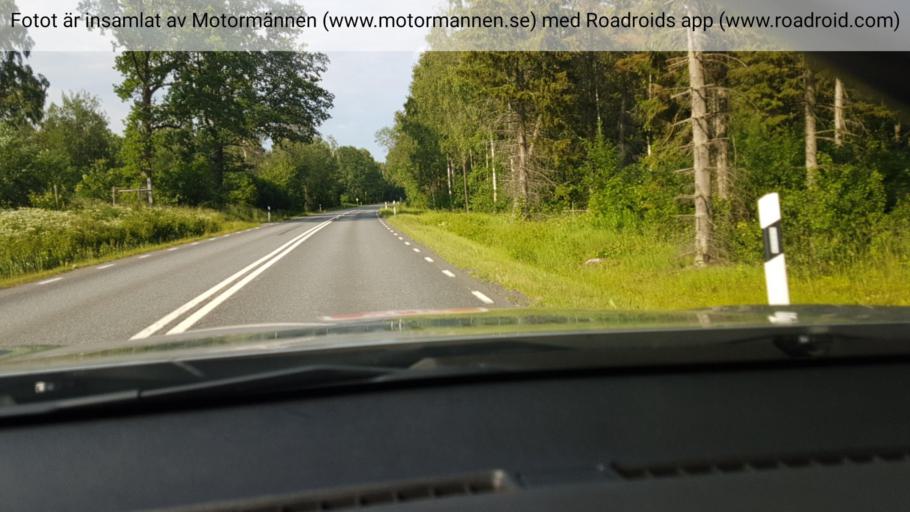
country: SE
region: Vaestra Goetaland
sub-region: Hjo Kommun
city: Hjo
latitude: 58.1149
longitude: 14.2103
